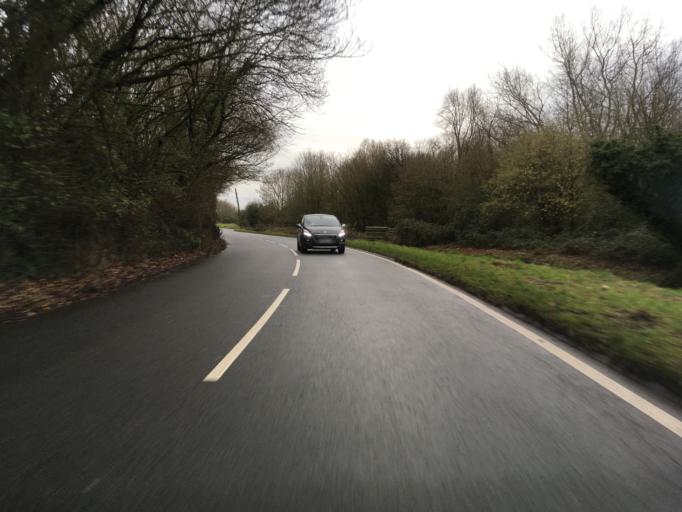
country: GB
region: Wales
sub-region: Newport
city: Nash
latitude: 51.5646
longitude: -2.9492
